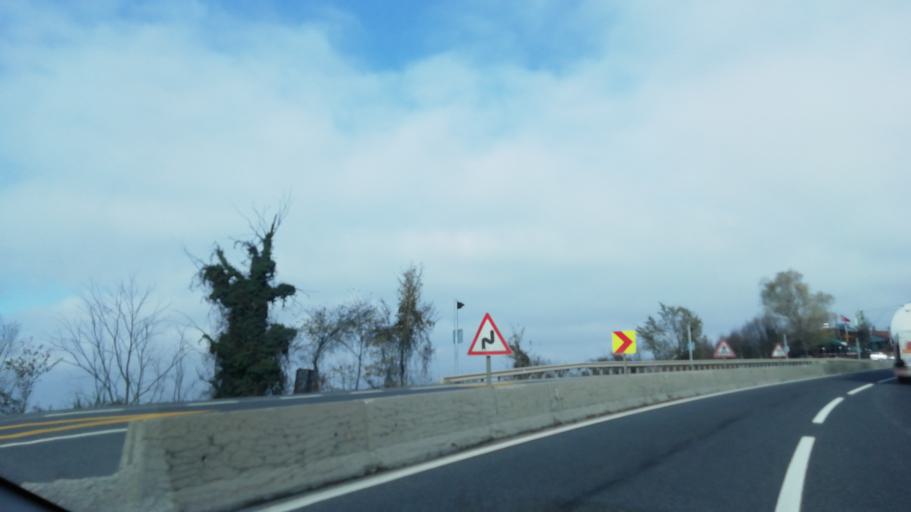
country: TR
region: Duzce
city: Kaynasli
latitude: 40.7510
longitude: 31.3834
